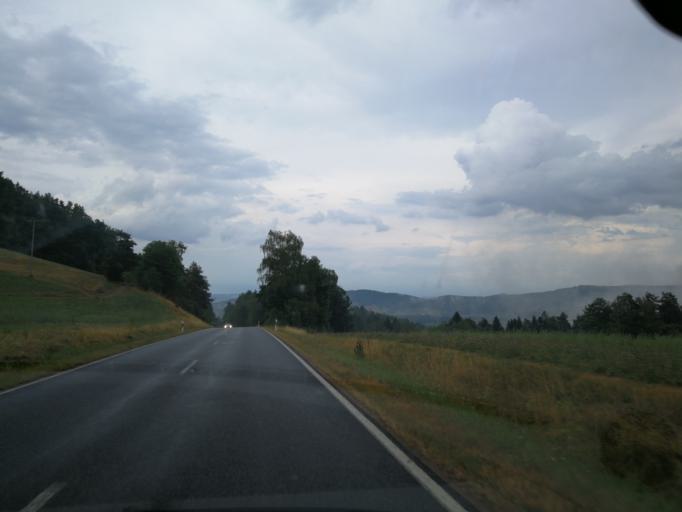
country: DE
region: Bavaria
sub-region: Upper Palatinate
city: Michelsneukirchen
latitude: 49.1471
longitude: 12.5731
